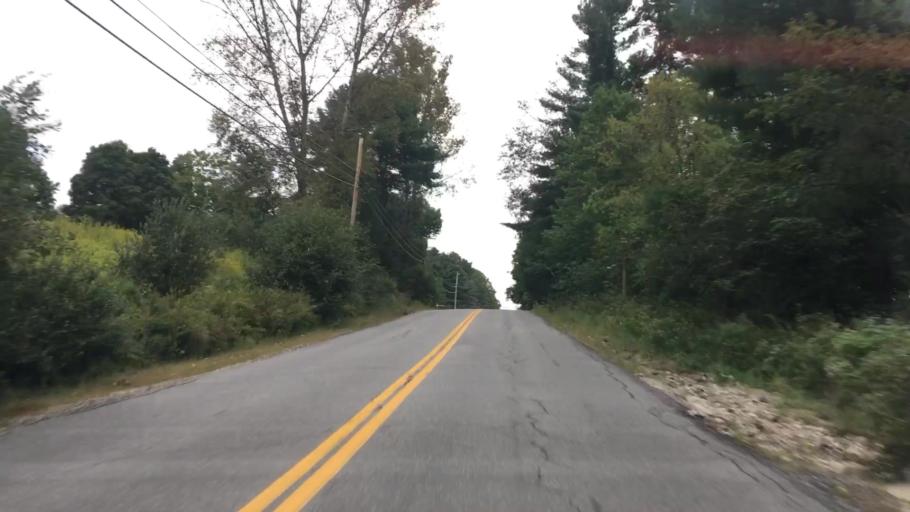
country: US
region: Maine
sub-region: Cumberland County
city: Freeport
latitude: 43.8932
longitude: -70.1864
